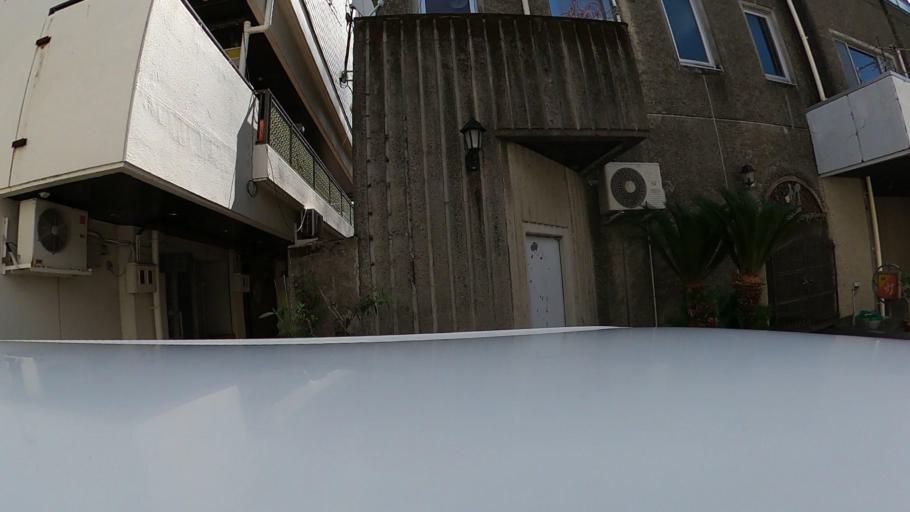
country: JP
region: Miyazaki
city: Tsuma
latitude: 32.1106
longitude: 131.4054
